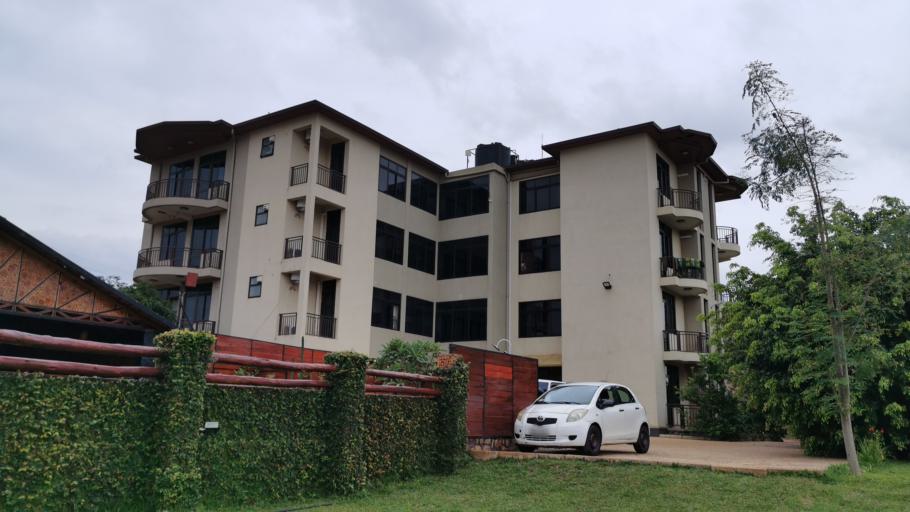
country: RW
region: Kigali
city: Kigali
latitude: -1.9114
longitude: 30.0836
